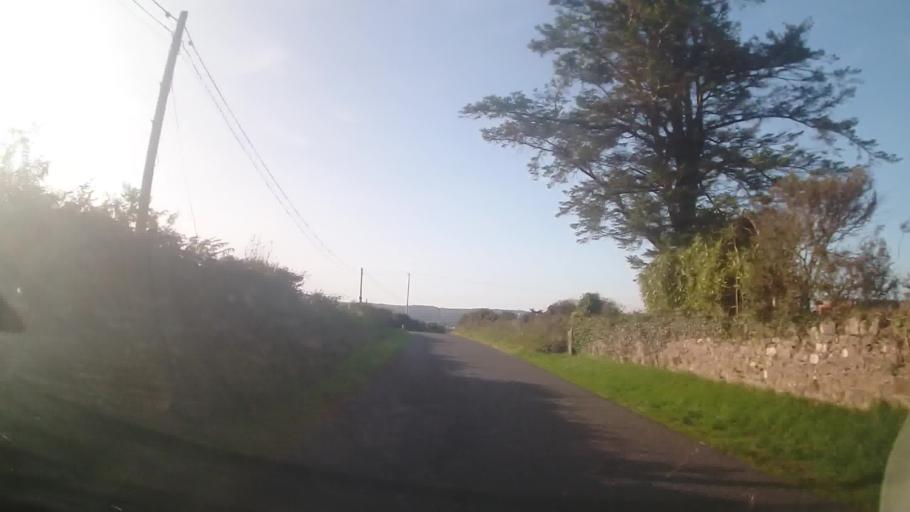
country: GB
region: Wales
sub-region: Pembrokeshire
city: Fishguard
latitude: 51.9883
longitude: -4.9619
